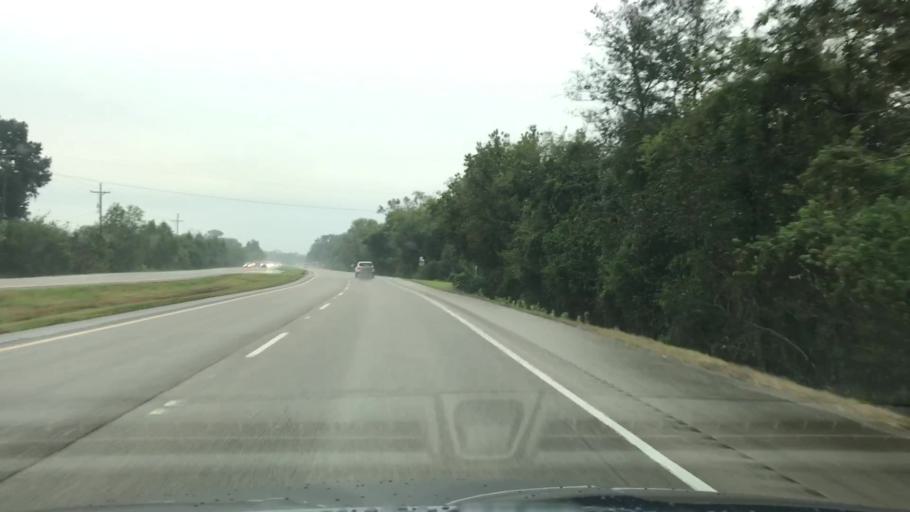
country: US
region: Louisiana
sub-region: Saint Charles Parish
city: Paradis
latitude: 29.8544
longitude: -90.4479
